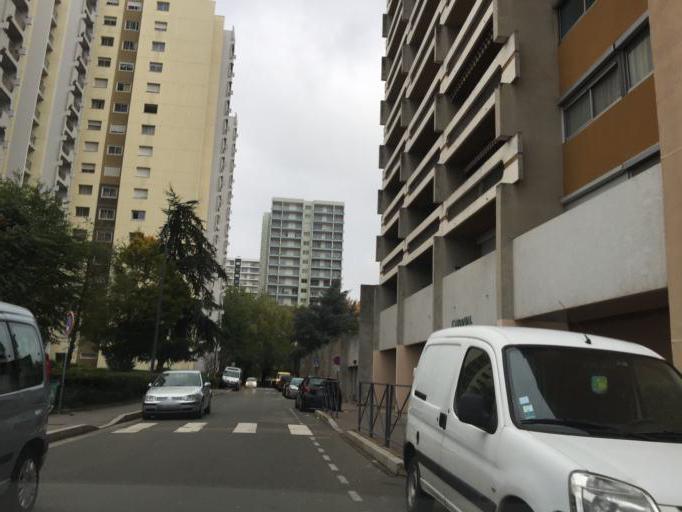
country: FR
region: Rhone-Alpes
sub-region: Departement de la Loire
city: Saint-Priest-en-Jarez
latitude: 45.4557
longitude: 4.3842
